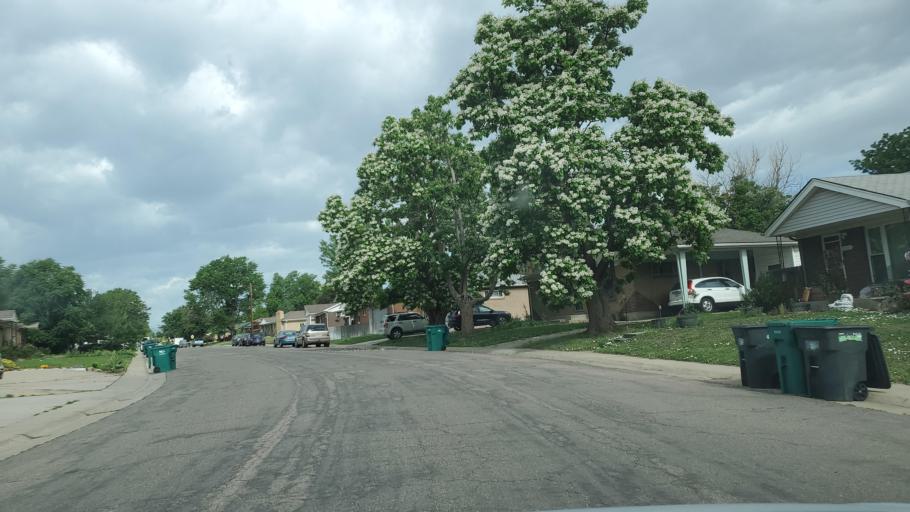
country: US
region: Colorado
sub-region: Adams County
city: Twin Lakes
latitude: 39.8307
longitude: -105.0111
